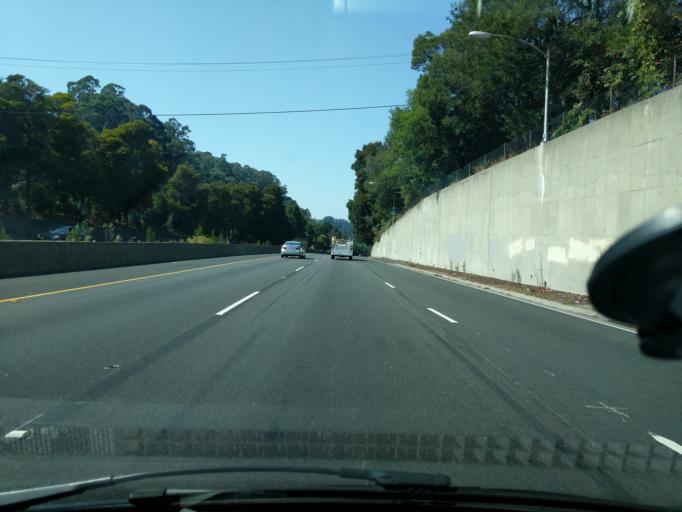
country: US
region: California
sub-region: Alameda County
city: Piedmont
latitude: 37.8117
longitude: -122.1986
